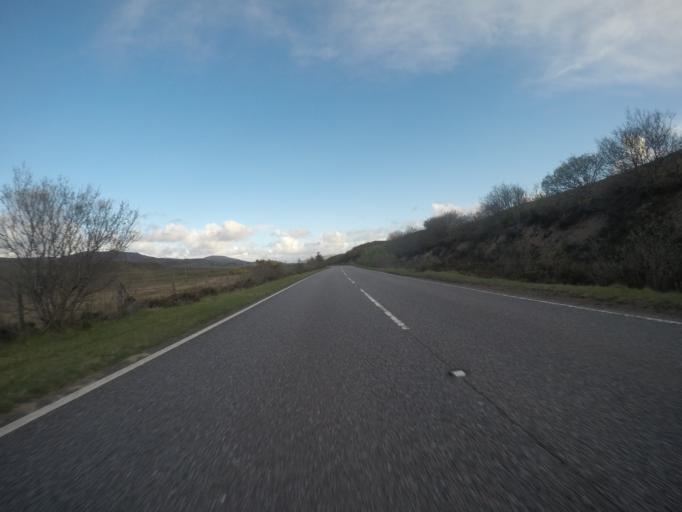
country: GB
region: Scotland
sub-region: Highland
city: Isle of Skye
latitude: 57.5073
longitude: -6.3361
